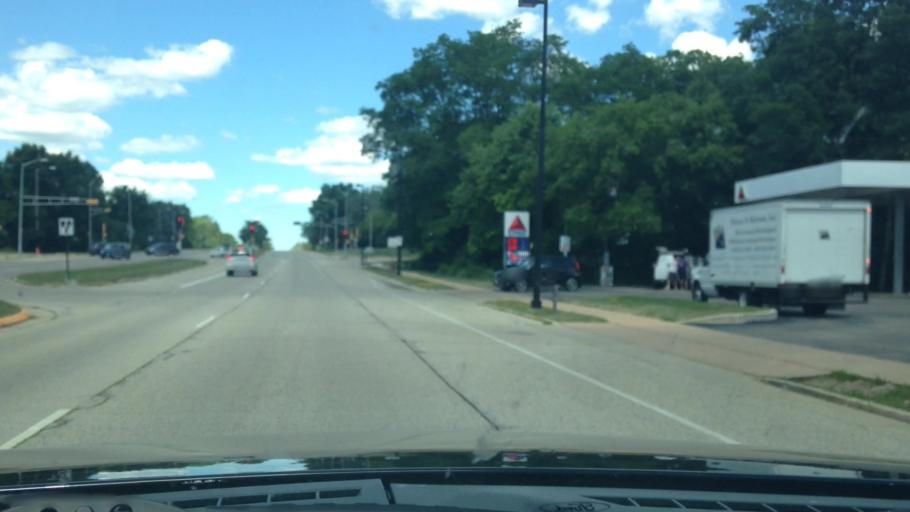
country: US
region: Wisconsin
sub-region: Waukesha County
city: Menomonee Falls
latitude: 43.1548
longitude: -88.0830
